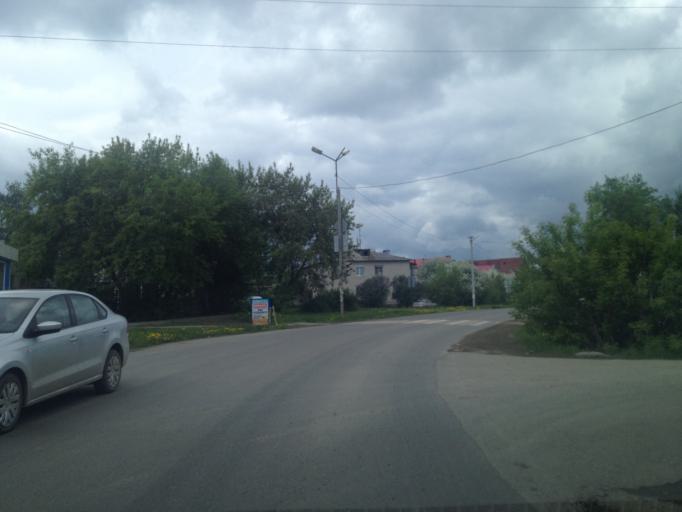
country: RU
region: Sverdlovsk
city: Aramil
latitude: 56.6852
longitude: 60.8450
